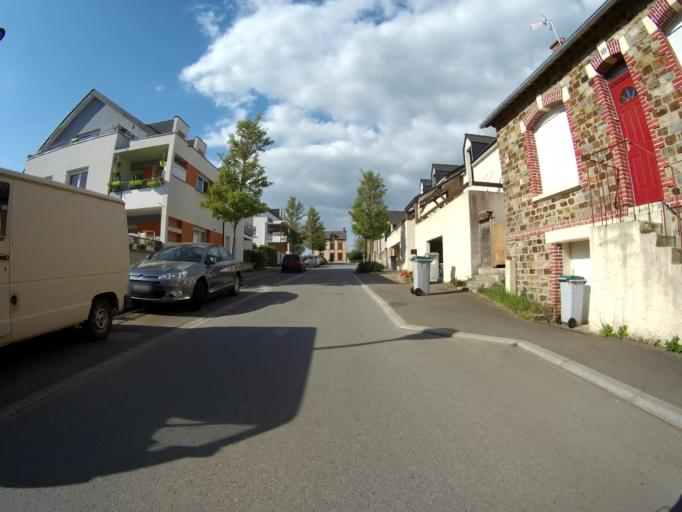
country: FR
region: Brittany
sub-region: Departement d'Ille-et-Vilaine
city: Vern-sur-Seiche
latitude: 48.0475
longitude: -1.5961
